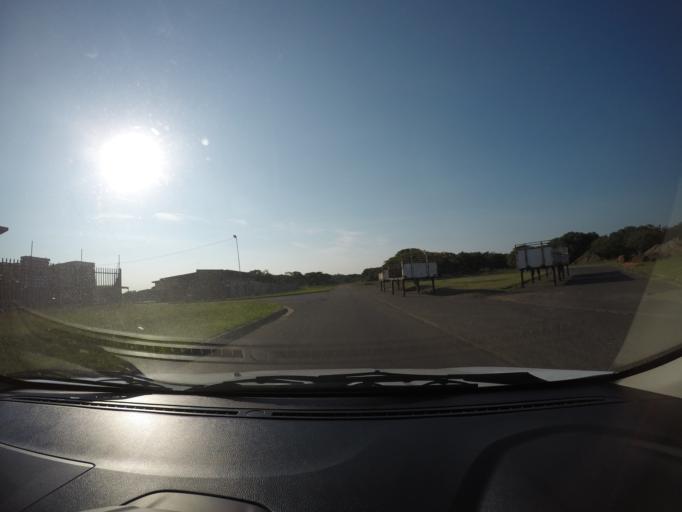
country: ZA
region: KwaZulu-Natal
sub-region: uThungulu District Municipality
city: Richards Bay
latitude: -28.7503
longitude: 32.0162
